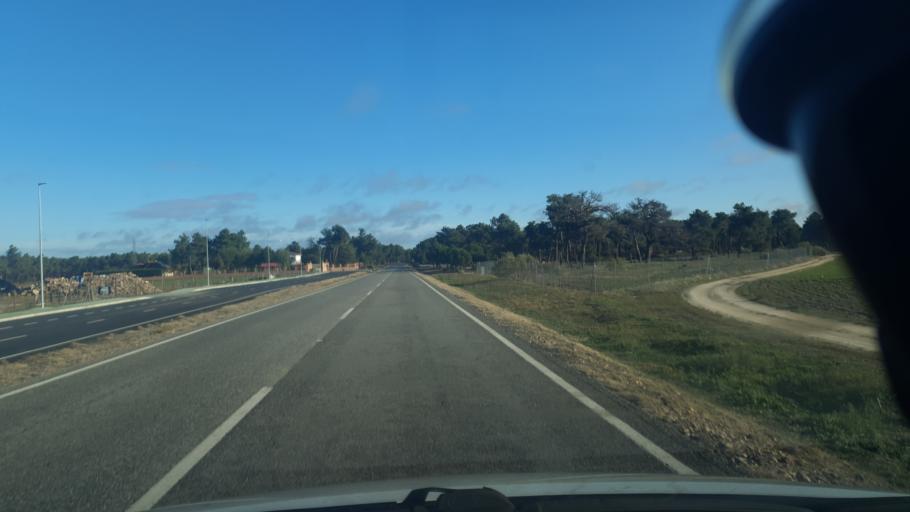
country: ES
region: Castille and Leon
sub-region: Provincia de Avila
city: Tinosillos
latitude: 40.9417
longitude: -4.7222
